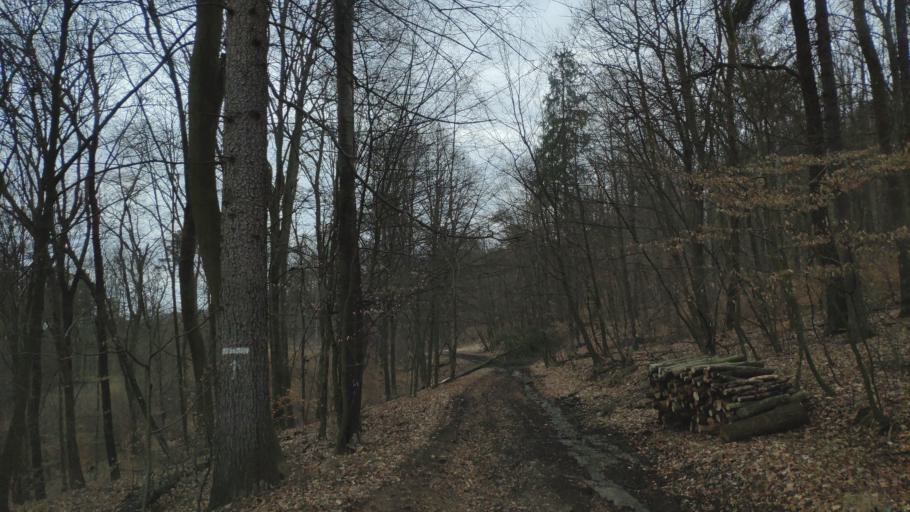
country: SK
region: Presovsky
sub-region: Okres Presov
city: Presov
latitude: 49.0709
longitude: 21.2821
